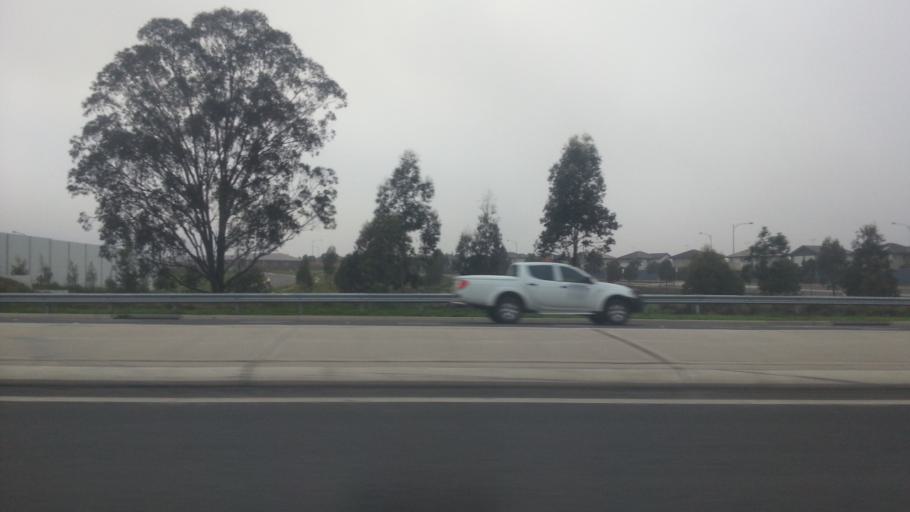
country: AU
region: New South Wales
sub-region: Camden
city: Narellan Vale
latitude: -34.0605
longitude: 150.7277
